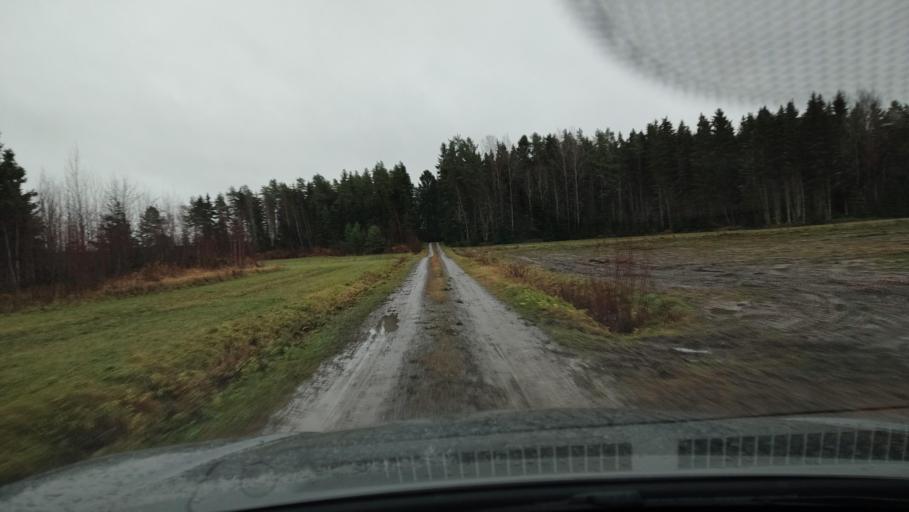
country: FI
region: Ostrobothnia
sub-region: Sydosterbotten
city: Kristinestad
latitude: 62.2329
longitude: 21.5473
